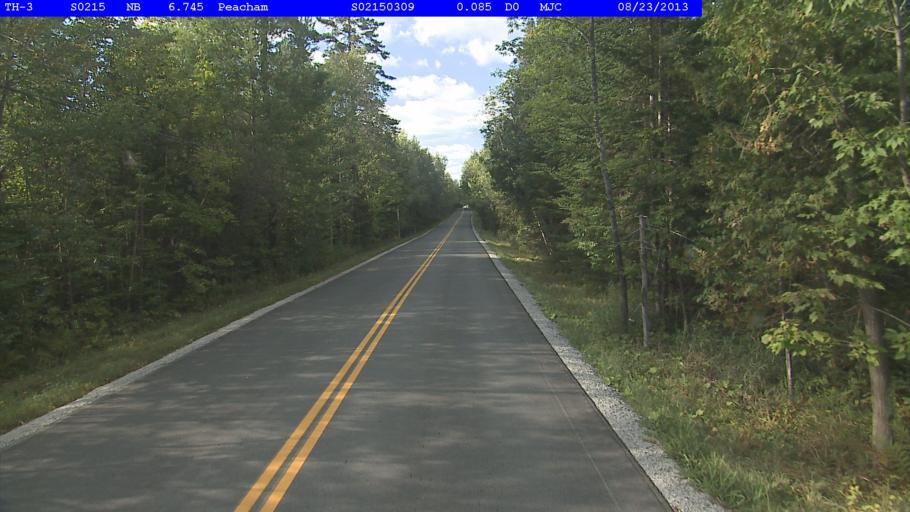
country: US
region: Vermont
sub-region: Caledonia County
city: Saint Johnsbury
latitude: 44.2991
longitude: -72.1634
